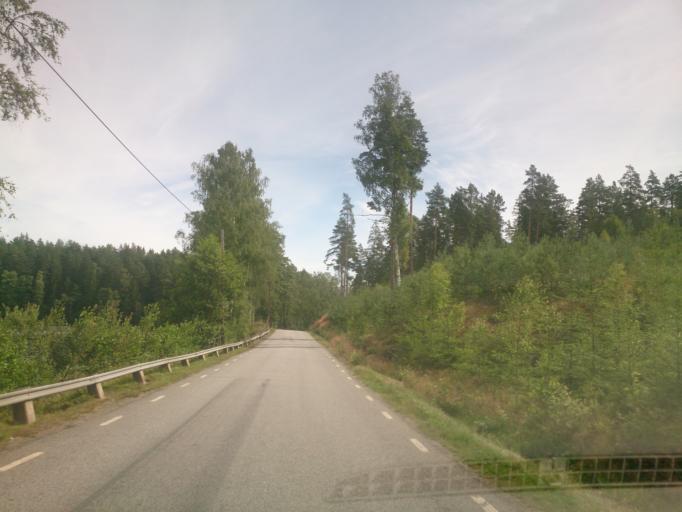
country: SE
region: OEstergoetland
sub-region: Valdemarsviks Kommun
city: Gusum
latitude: 58.3158
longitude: 16.3278
